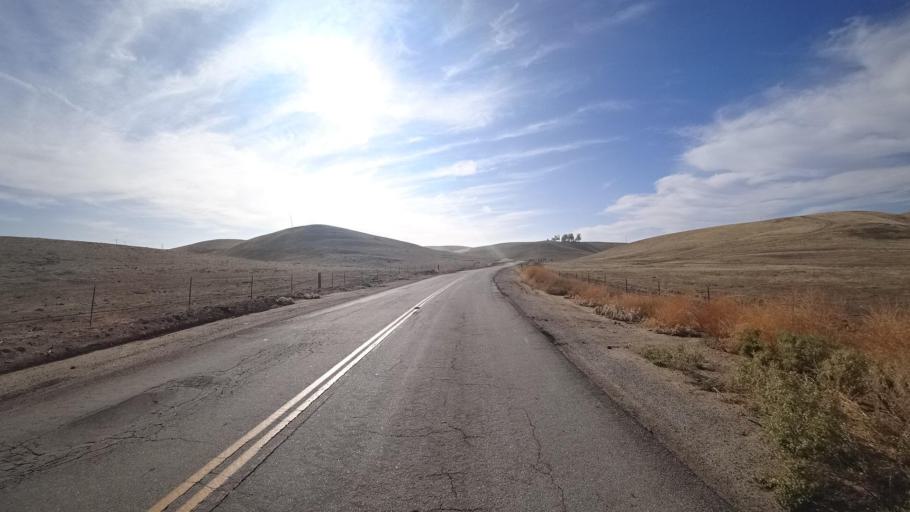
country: US
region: California
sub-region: Kern County
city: Oildale
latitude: 35.6214
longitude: -118.9870
